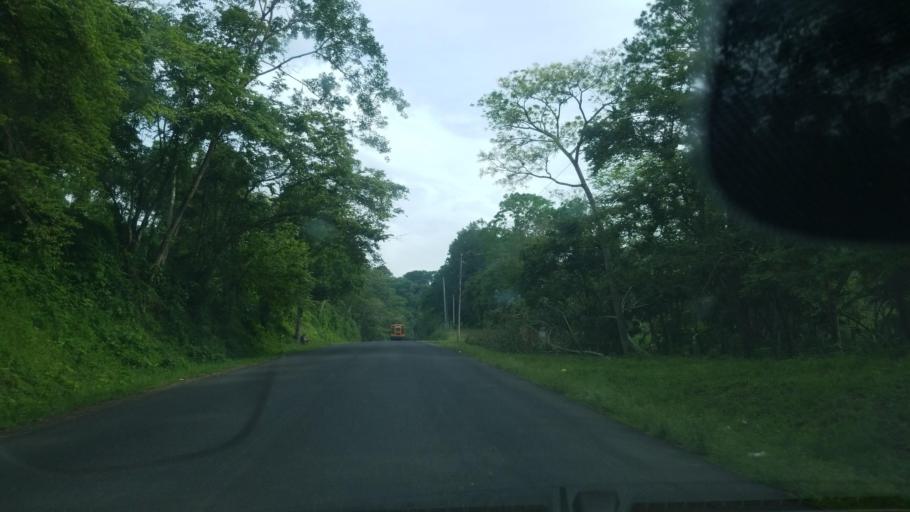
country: HN
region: Santa Barbara
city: Petoa
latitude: 15.2217
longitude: -88.2675
